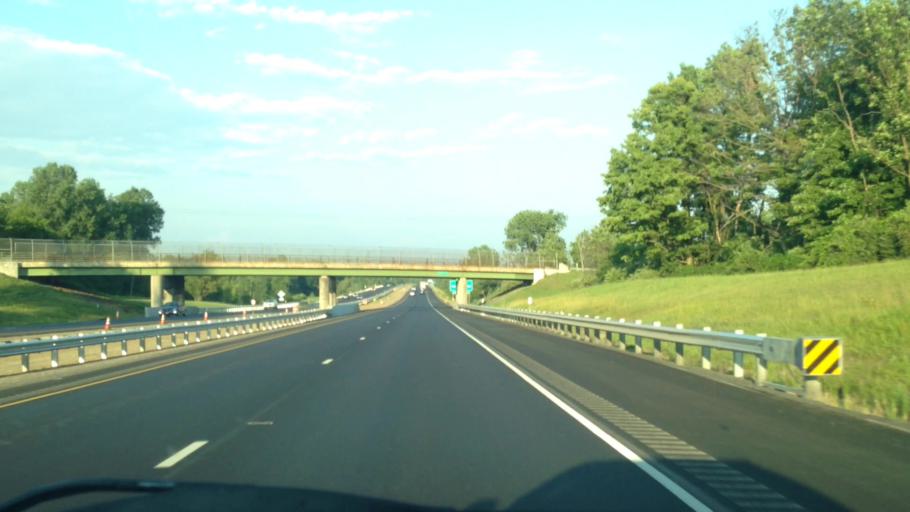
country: US
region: New York
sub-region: Oneida County
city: Clark Mills
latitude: 43.1280
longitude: -75.4397
